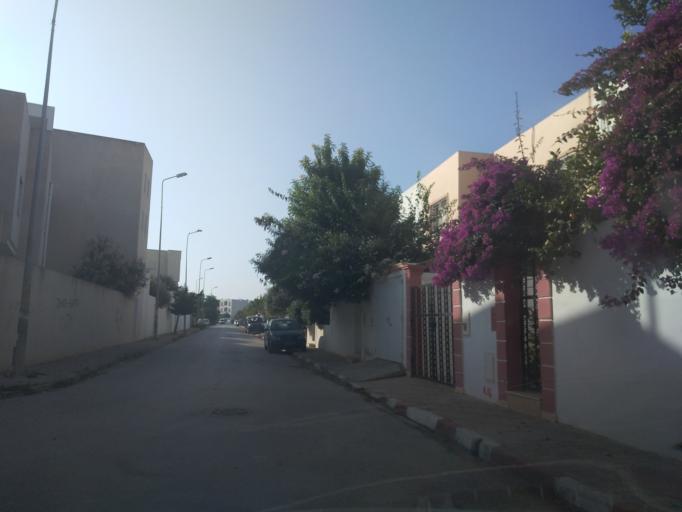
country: TN
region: Manouba
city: Manouba
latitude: 36.7917
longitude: 10.0857
